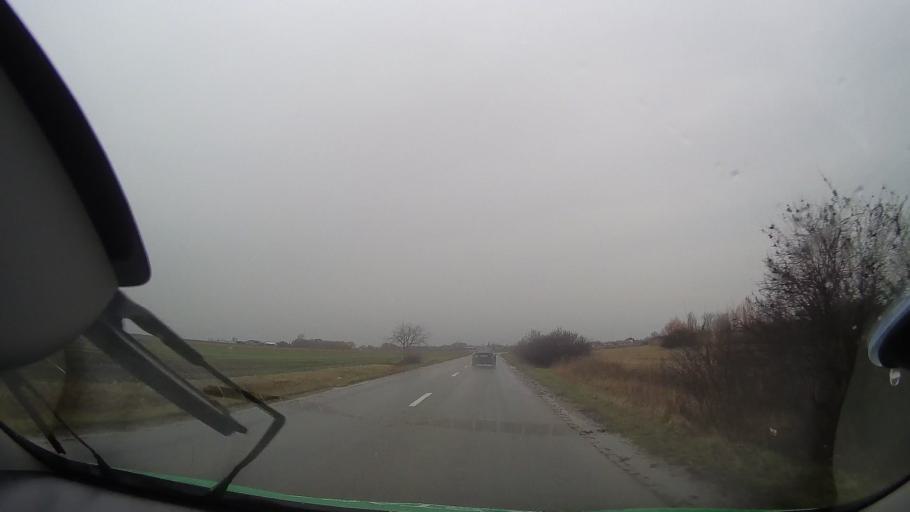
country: RO
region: Bihor
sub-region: Comuna Madaras
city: Madaras
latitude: 46.7934
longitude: 21.6901
